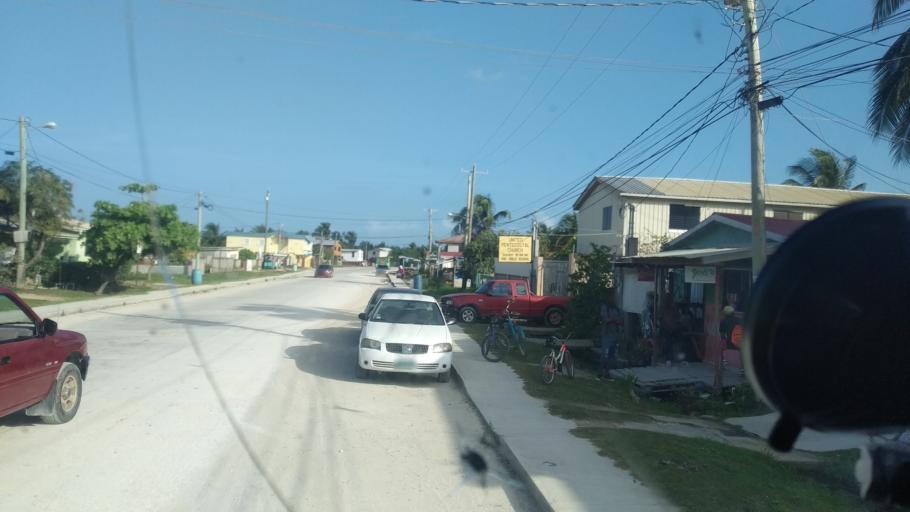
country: BZ
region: Belize
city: Belize City
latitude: 17.4840
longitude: -88.2013
